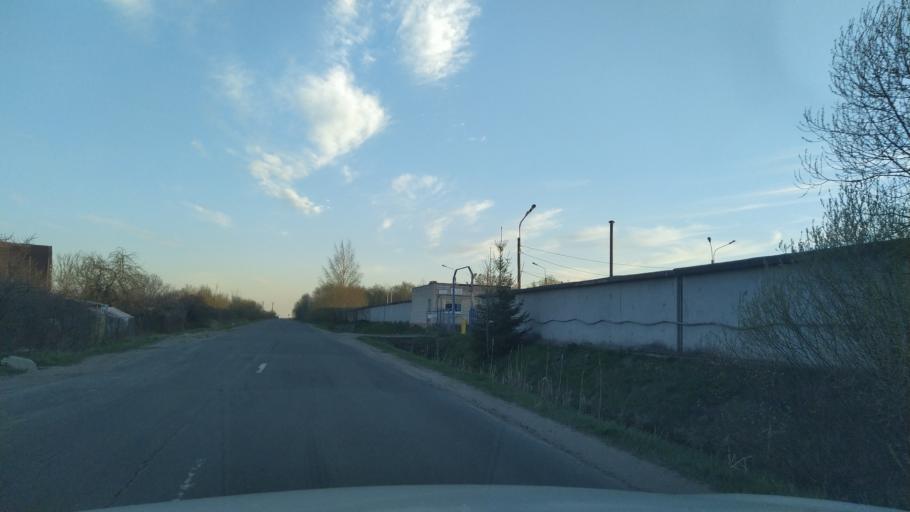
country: RU
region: St.-Petersburg
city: Pushkin
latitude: 59.6905
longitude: 30.3962
